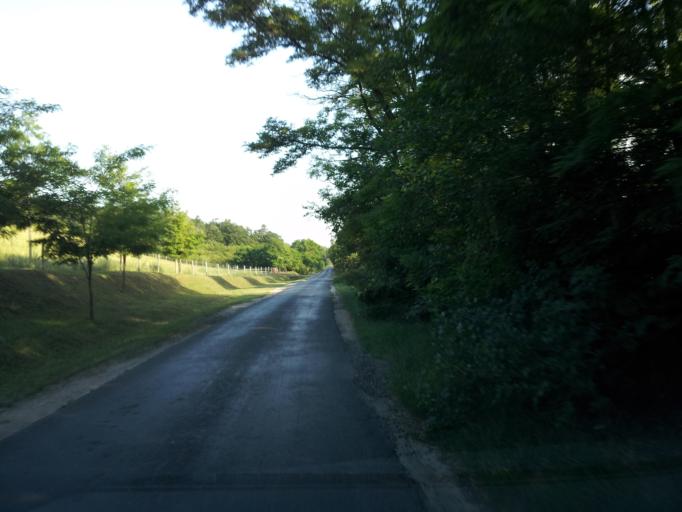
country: HU
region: Fejer
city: Many
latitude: 47.5460
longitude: 18.5879
